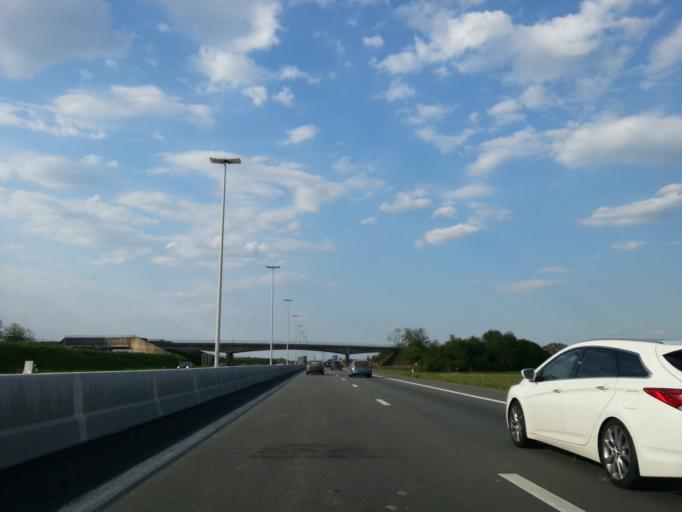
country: BE
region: Flanders
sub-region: Provincie Antwerpen
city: Hoogstraten
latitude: 51.4306
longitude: 4.7112
